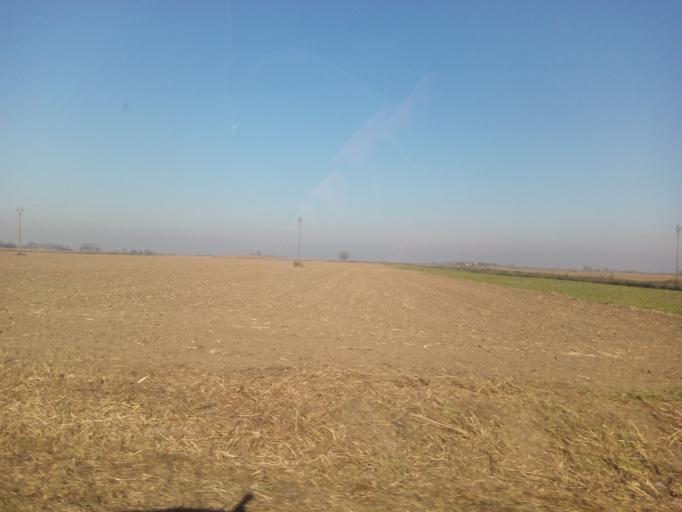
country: RS
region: Autonomna Pokrajina Vojvodina
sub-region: Juznobacki Okrug
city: Beocin
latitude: 45.2411
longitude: 19.6631
